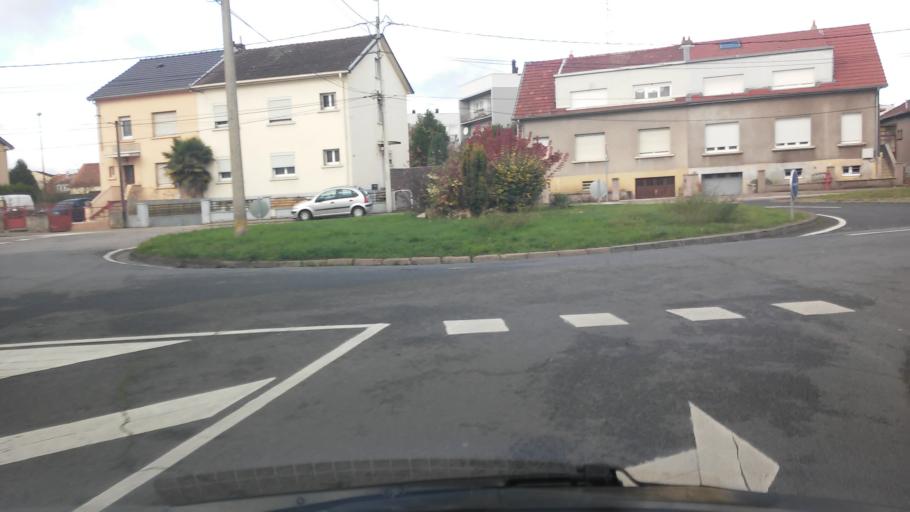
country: FR
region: Lorraine
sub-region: Departement de la Moselle
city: Talange
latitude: 49.2340
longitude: 6.1724
